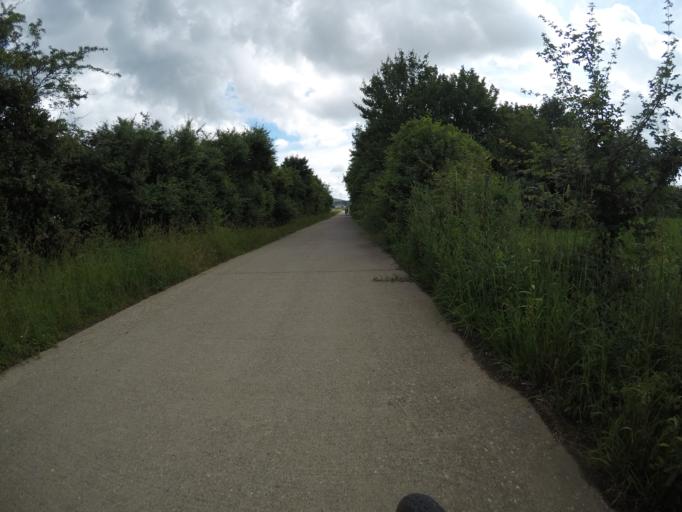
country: DE
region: Baden-Wuerttemberg
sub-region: Regierungsbezirk Stuttgart
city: Salach
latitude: 48.6981
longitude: 9.7241
